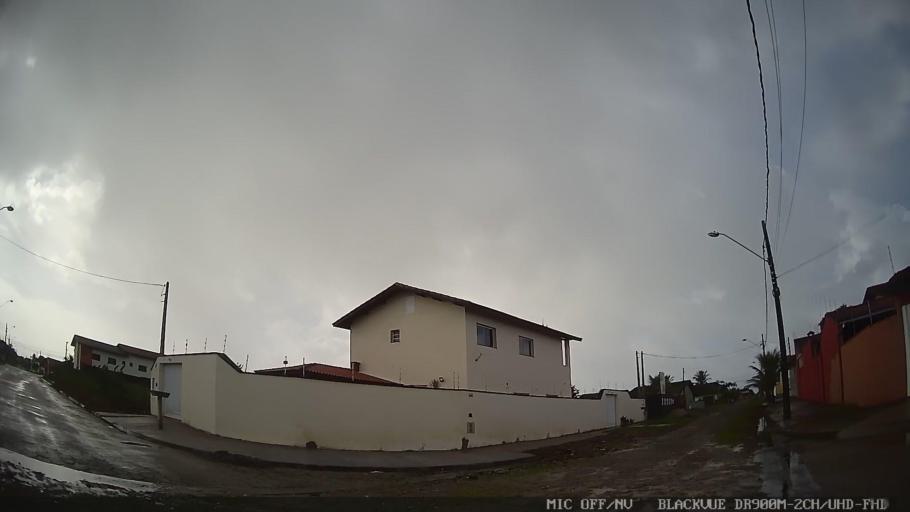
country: BR
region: Sao Paulo
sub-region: Itanhaem
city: Itanhaem
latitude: -24.2018
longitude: -46.8333
